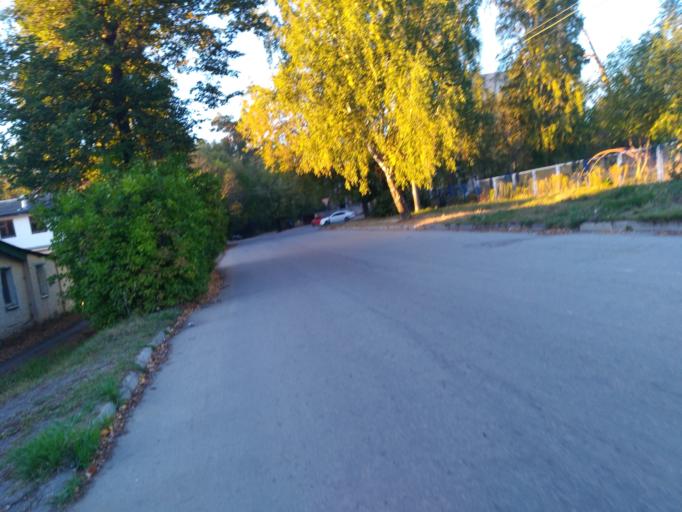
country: RU
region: Kaluga
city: Kaluga
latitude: 54.5335
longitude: 36.2551
